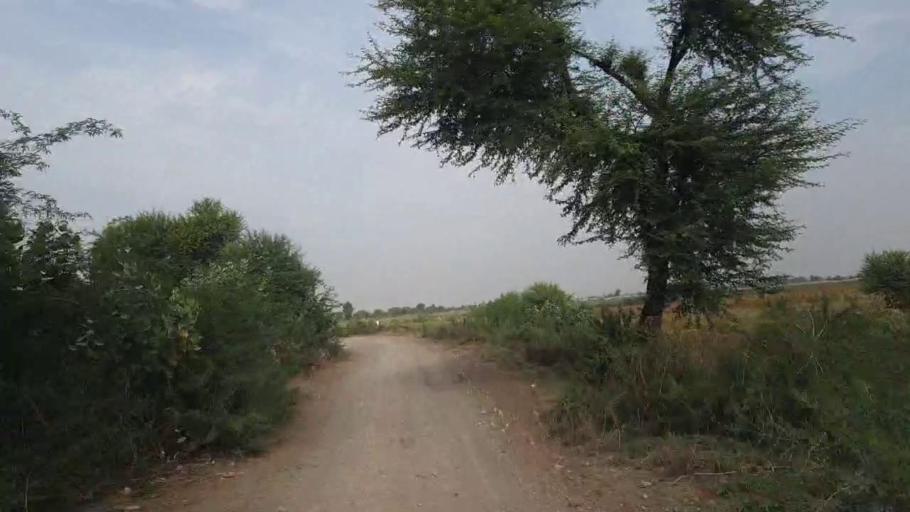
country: PK
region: Sindh
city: Rajo Khanani
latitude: 24.9722
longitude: 68.9960
